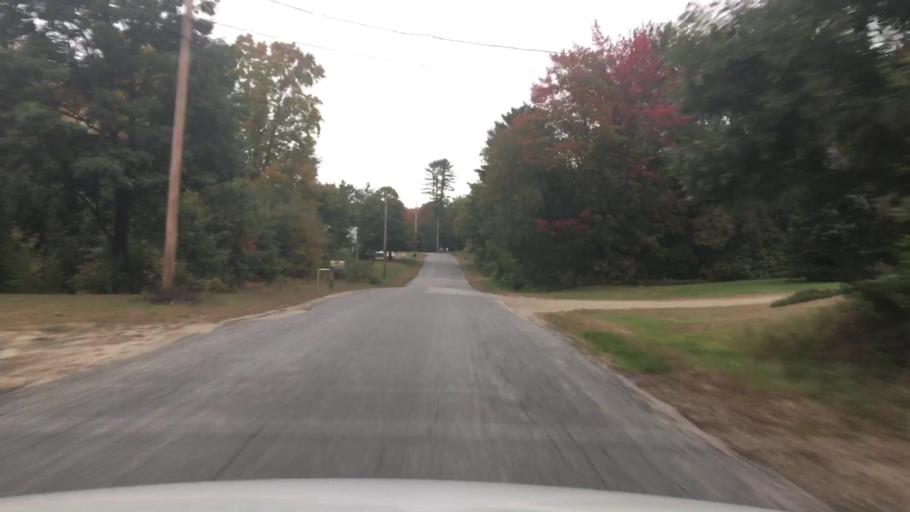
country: US
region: Maine
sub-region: Oxford County
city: Bethel
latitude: 44.4684
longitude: -70.7847
